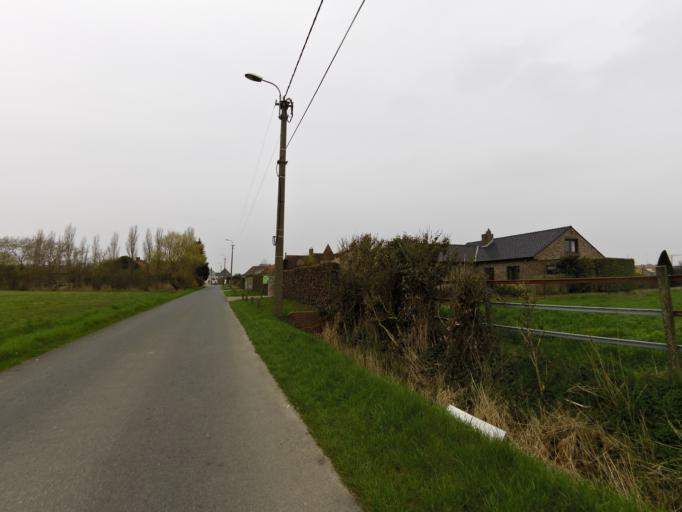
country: BE
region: Flanders
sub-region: Provincie West-Vlaanderen
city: Middelkerke
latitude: 51.1716
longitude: 2.7977
